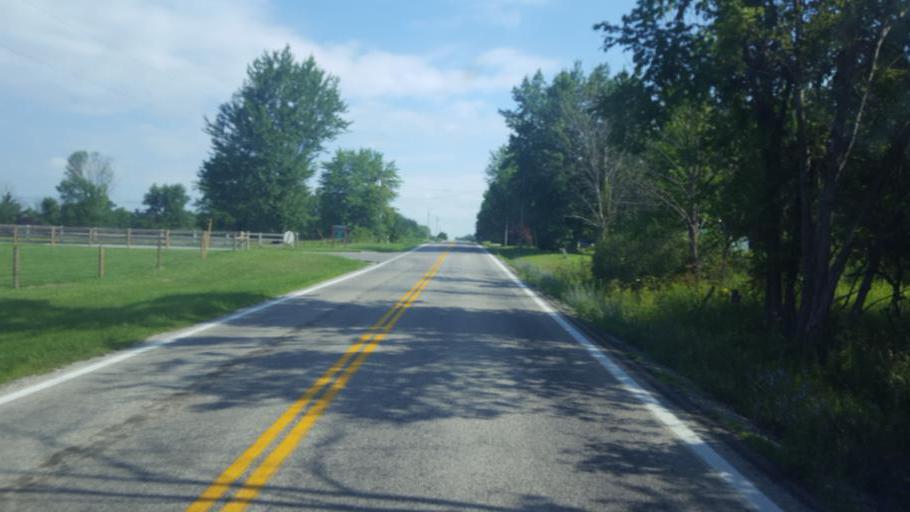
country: US
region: Ohio
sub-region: Crawford County
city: Galion
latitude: 40.6342
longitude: -82.7657
